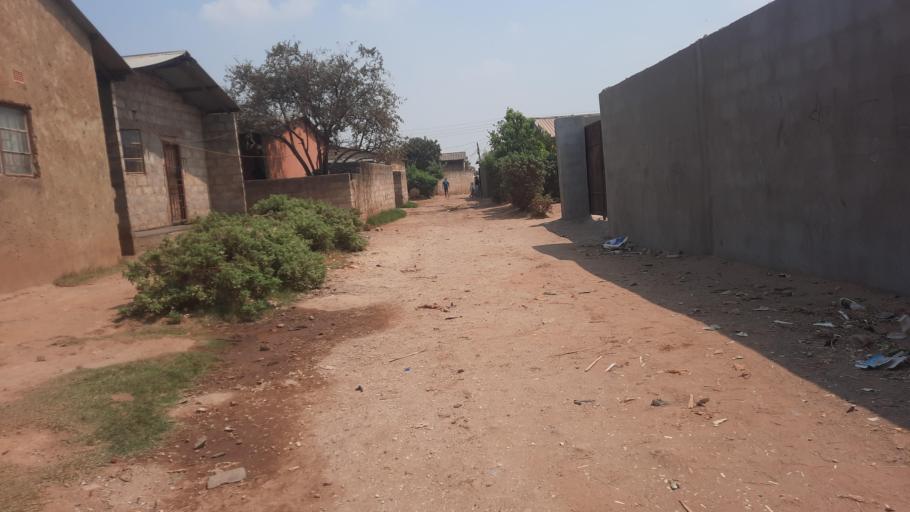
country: ZM
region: Lusaka
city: Lusaka
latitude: -15.4023
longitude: 28.3764
